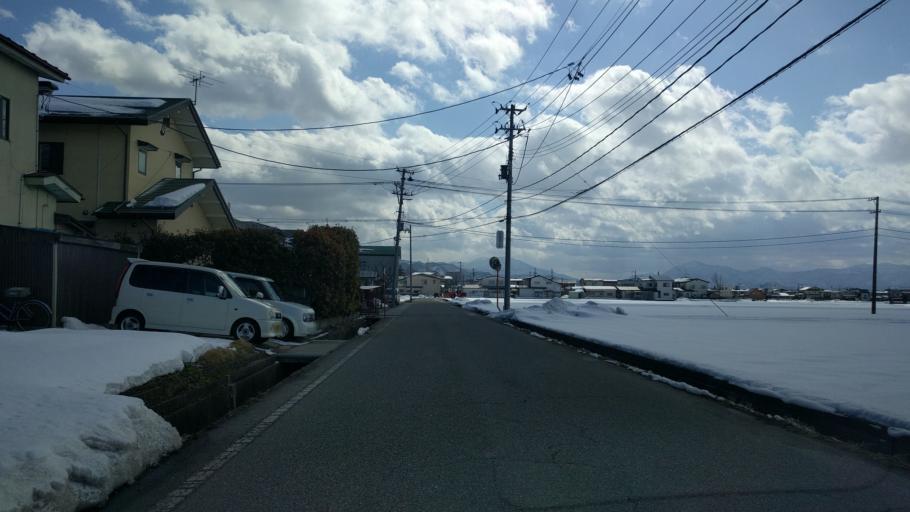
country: JP
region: Fukushima
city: Kitakata
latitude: 37.5119
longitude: 139.9253
